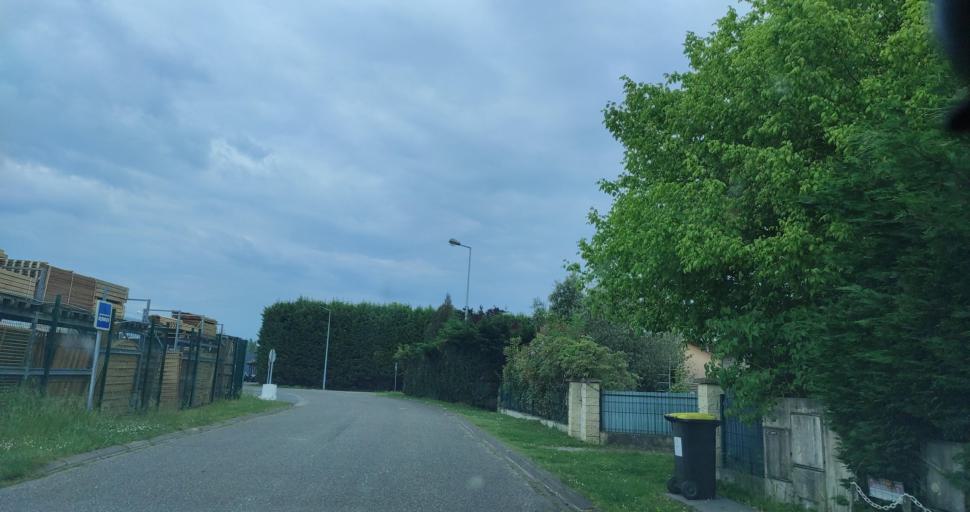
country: FR
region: Aquitaine
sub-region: Departement de la Gironde
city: Lanton
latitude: 44.7029
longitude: -1.0409
